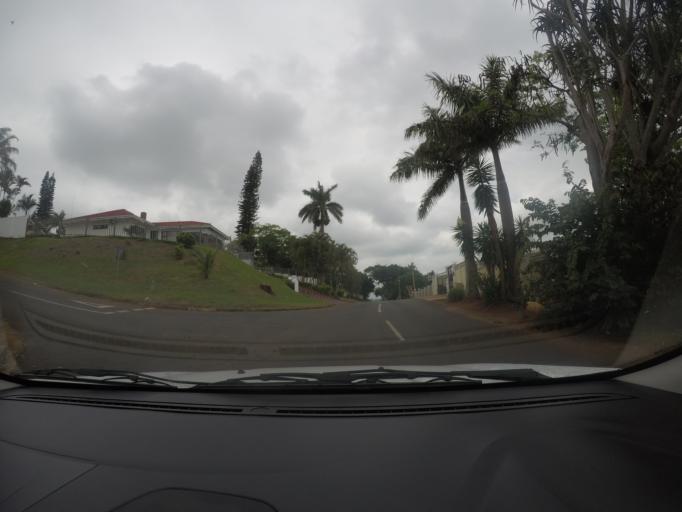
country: ZA
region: KwaZulu-Natal
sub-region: uThungulu District Municipality
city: Empangeni
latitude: -28.7554
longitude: 31.8862
